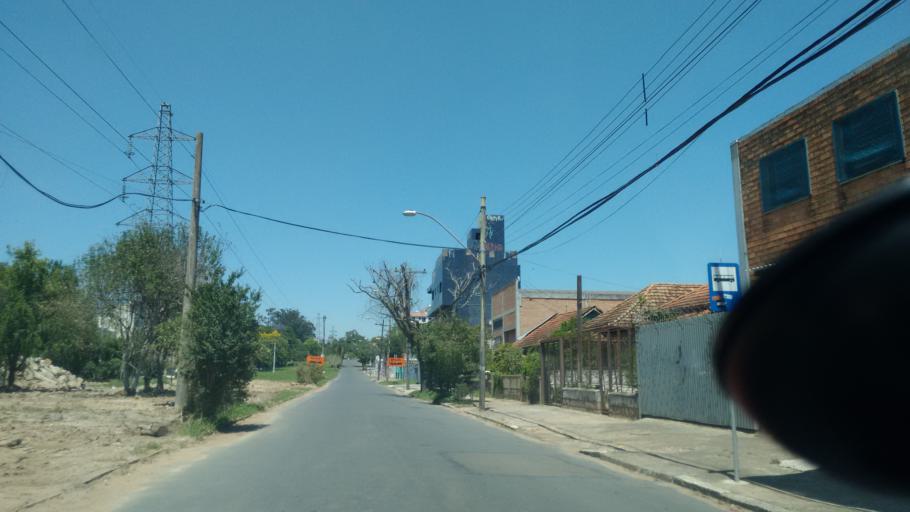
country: BR
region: Rio Grande do Sul
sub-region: Cachoeirinha
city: Cachoeirinha
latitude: -29.9986
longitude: -51.1260
